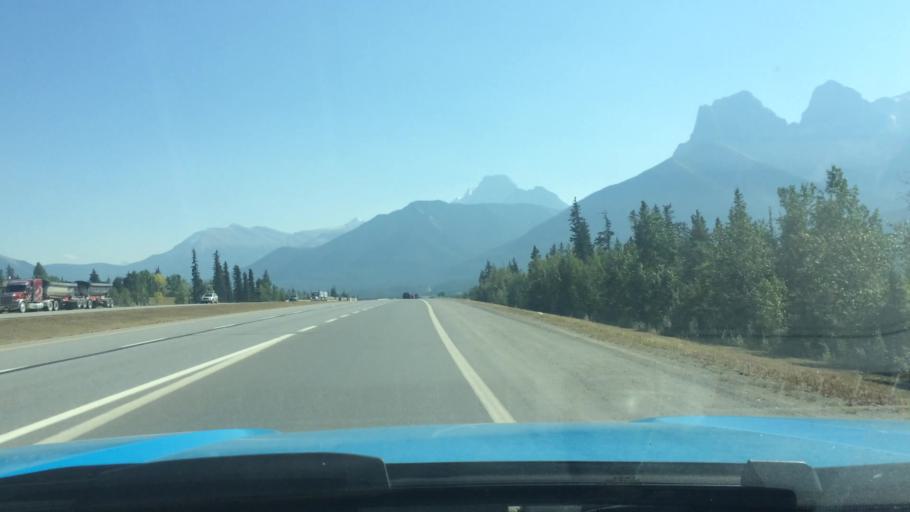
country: CA
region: Alberta
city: Canmore
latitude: 51.0848
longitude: -115.3393
